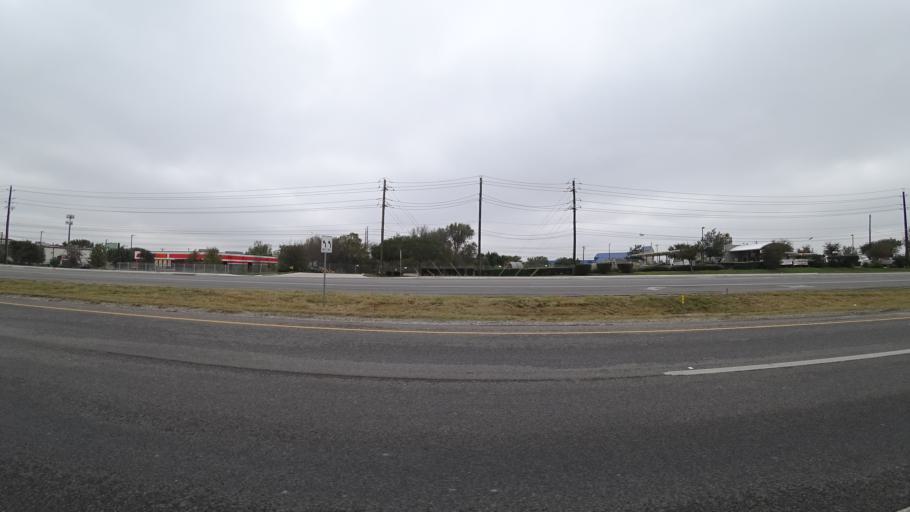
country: US
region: Texas
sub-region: Travis County
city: Pflugerville
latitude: 30.3879
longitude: -97.6499
